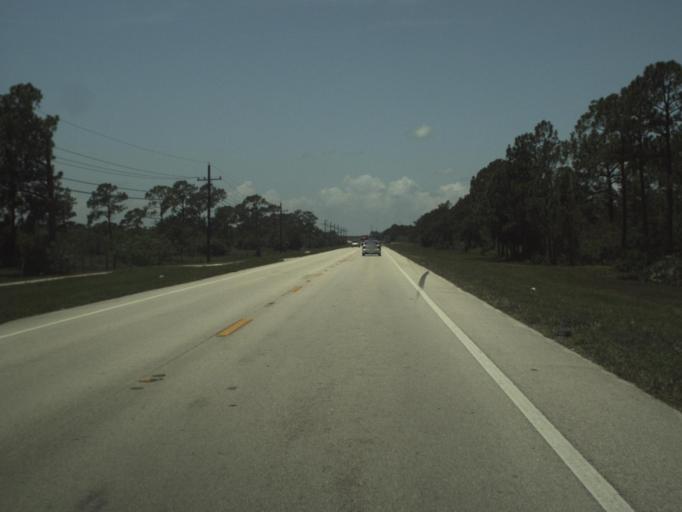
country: US
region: Florida
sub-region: Martin County
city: Palm City
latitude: 27.1619
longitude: -80.3744
